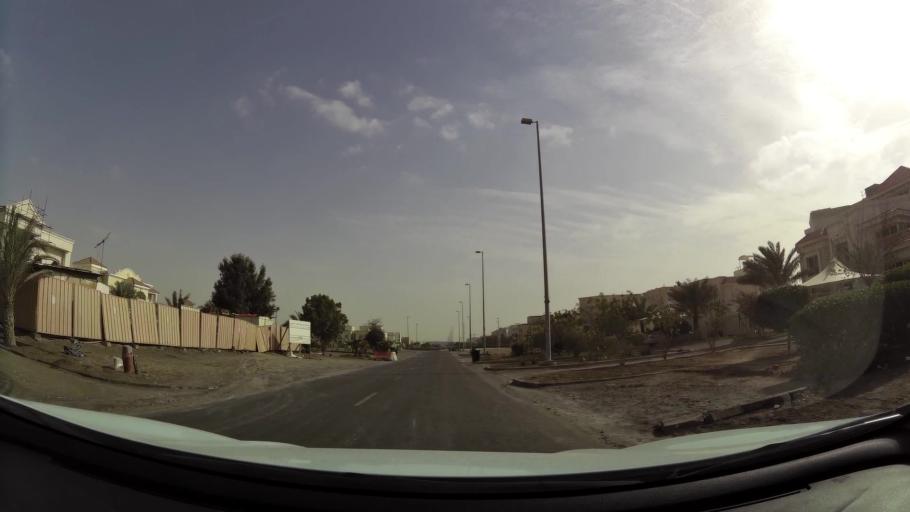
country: AE
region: Abu Dhabi
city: Abu Dhabi
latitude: 24.4129
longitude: 54.5776
